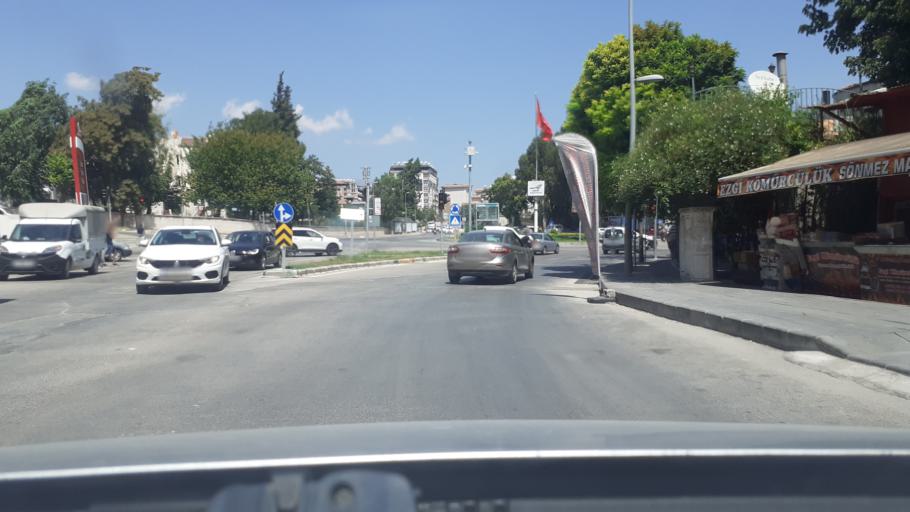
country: TR
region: Hatay
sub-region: Antakya Ilcesi
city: Antakya
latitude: 36.1990
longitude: 36.1543
